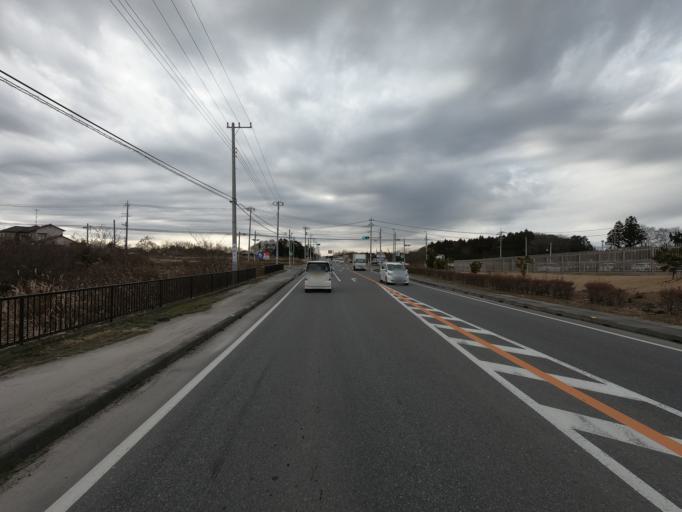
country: JP
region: Ibaraki
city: Ishioka
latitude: 36.0939
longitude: 140.3303
